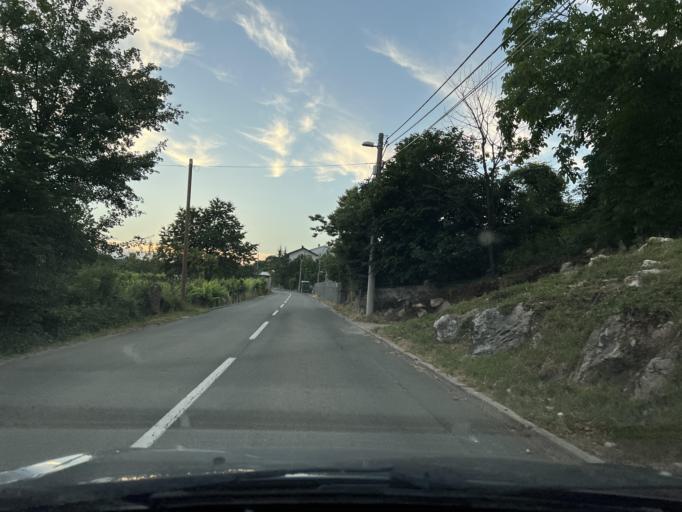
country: HR
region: Primorsko-Goranska
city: Marcelji
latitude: 45.3981
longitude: 14.3963
